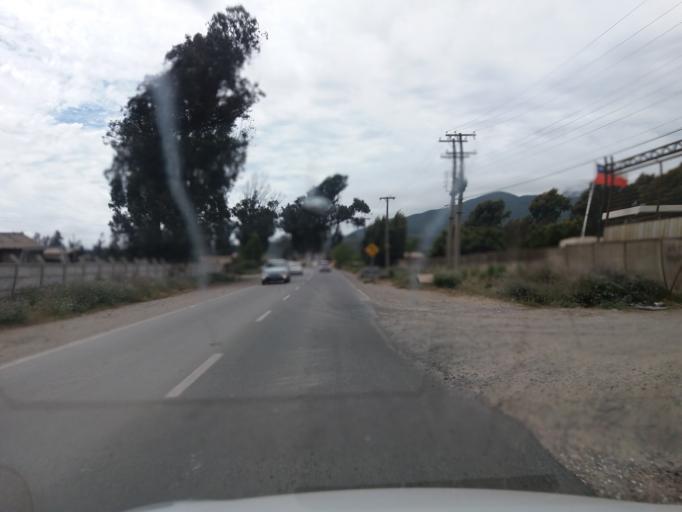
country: CL
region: Valparaiso
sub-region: Provincia de Marga Marga
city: Quilpue
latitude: -32.9288
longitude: -71.4401
